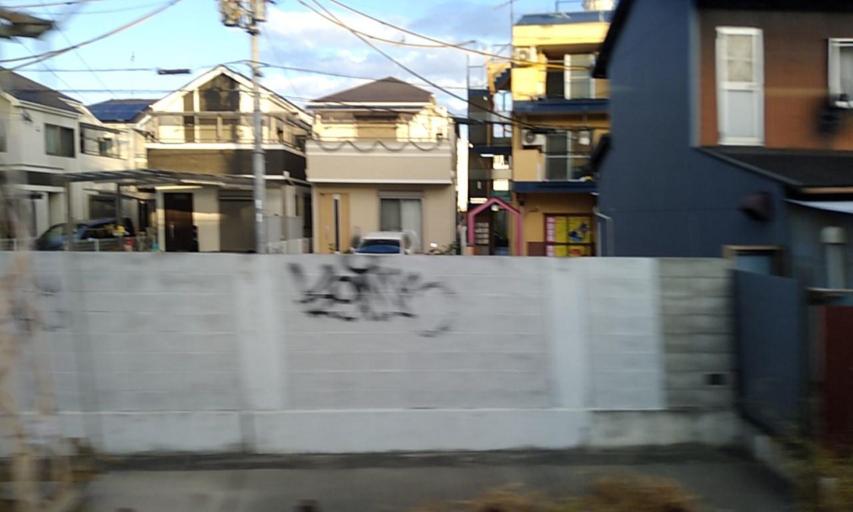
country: JP
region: Osaka
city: Sakai
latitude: 34.5726
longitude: 135.4842
